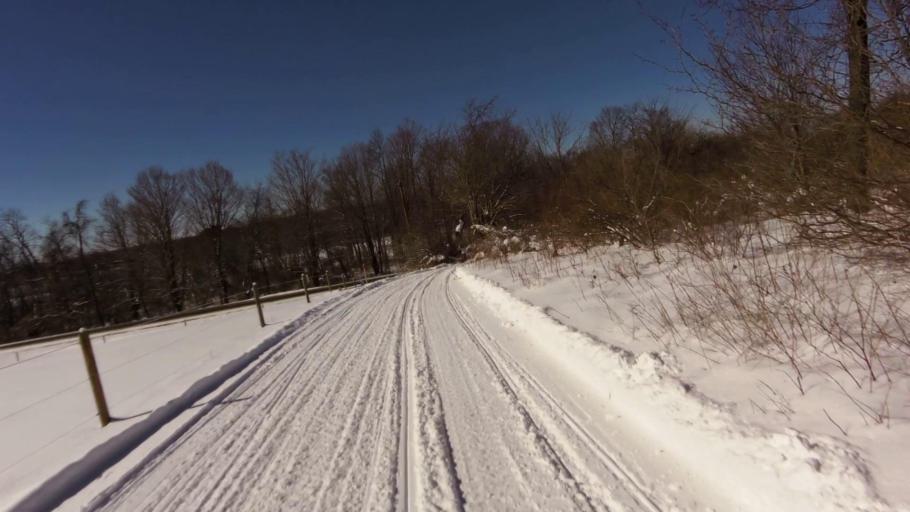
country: US
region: New York
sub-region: Chautauqua County
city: Mayville
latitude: 42.2234
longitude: -79.3974
